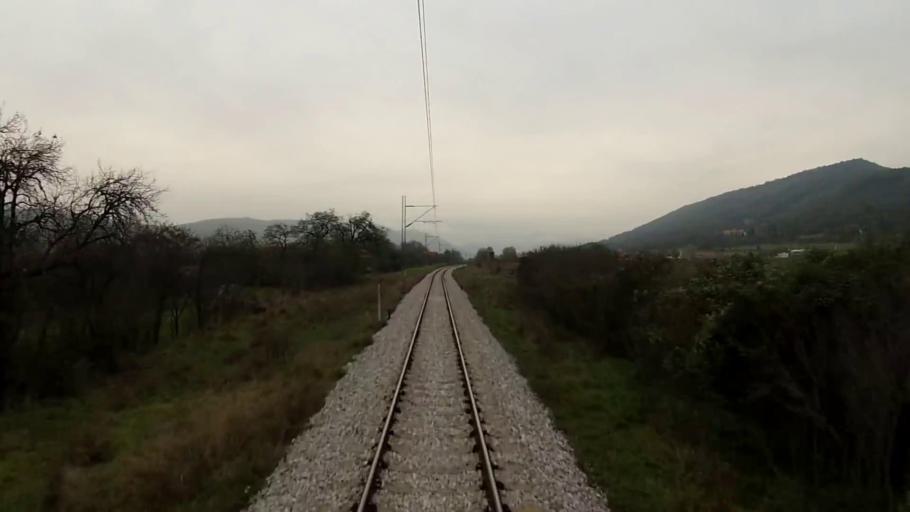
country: RS
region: Central Serbia
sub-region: Pirotski Okrug
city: Dimitrovgrad
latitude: 43.0036
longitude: 22.8162
